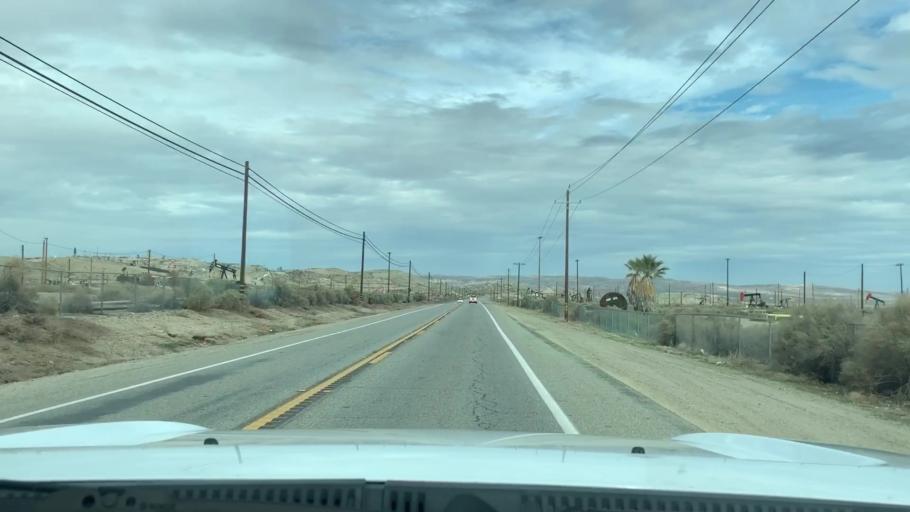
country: US
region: California
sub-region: Kern County
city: Maricopa
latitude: 35.0675
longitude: -119.4020
